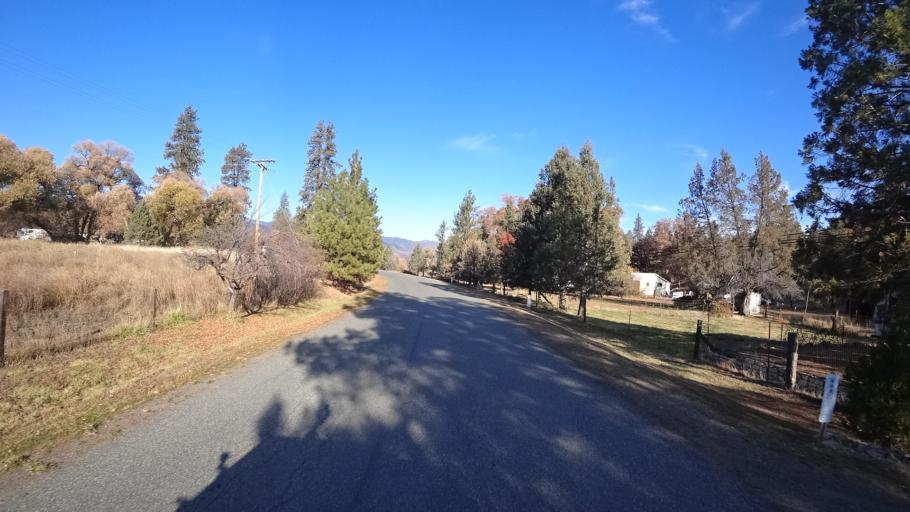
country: US
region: California
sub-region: Siskiyou County
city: Yreka
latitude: 41.6850
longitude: -122.6318
